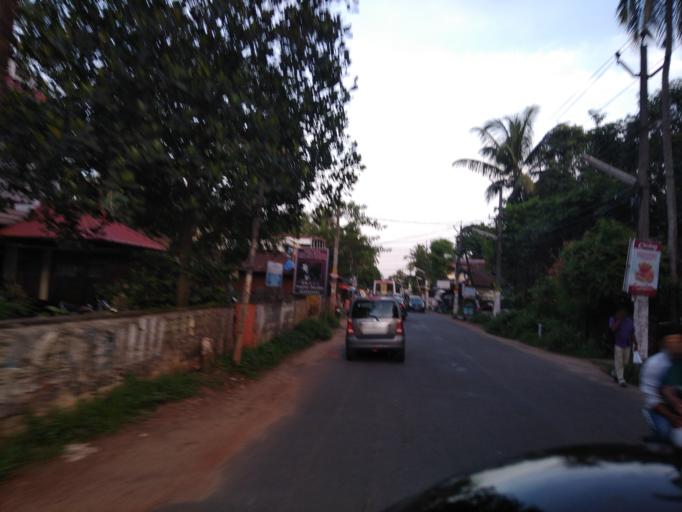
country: IN
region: Kerala
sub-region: Thrissur District
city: Trichur
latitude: 10.5308
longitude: 76.1852
